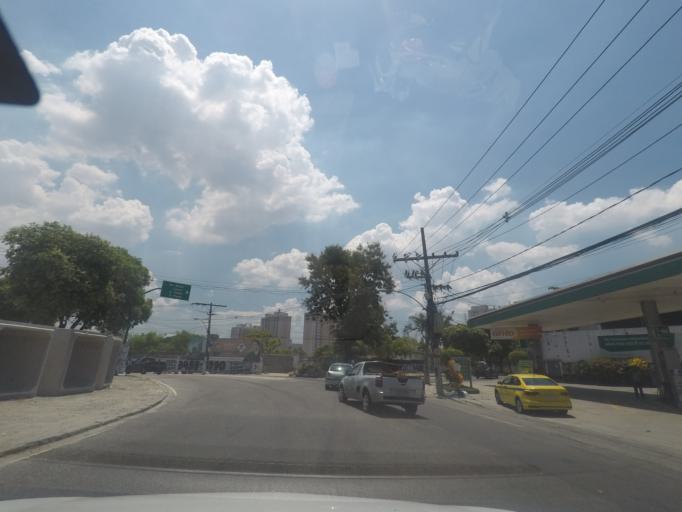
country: BR
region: Rio de Janeiro
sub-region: Duque De Caxias
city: Duque de Caxias
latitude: -22.8247
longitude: -43.3121
